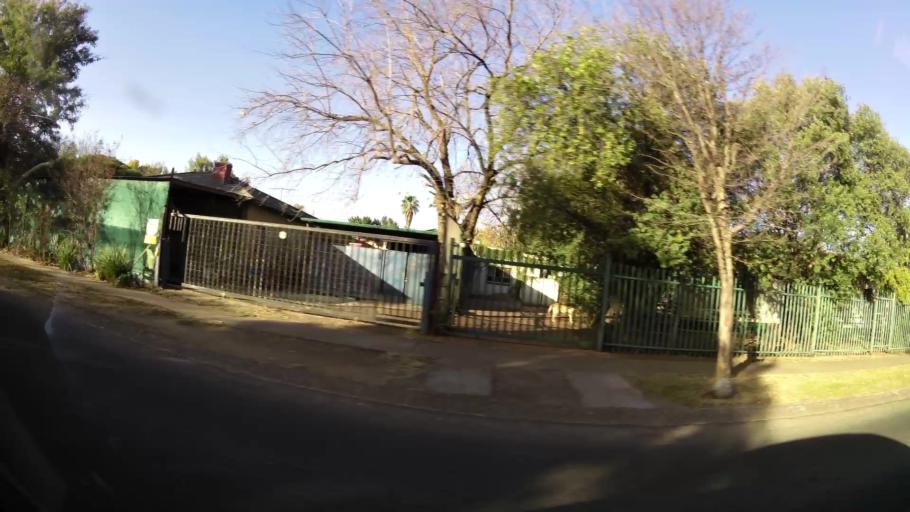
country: ZA
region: Gauteng
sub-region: City of Tshwane Metropolitan Municipality
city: Pretoria
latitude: -25.7158
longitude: 28.2099
